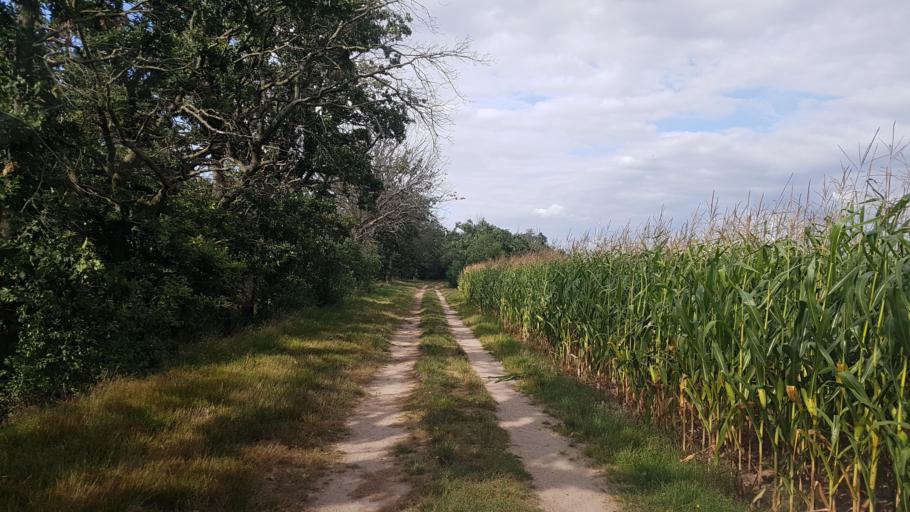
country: DE
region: Brandenburg
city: Bad Liebenwerda
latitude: 51.5096
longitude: 13.3012
